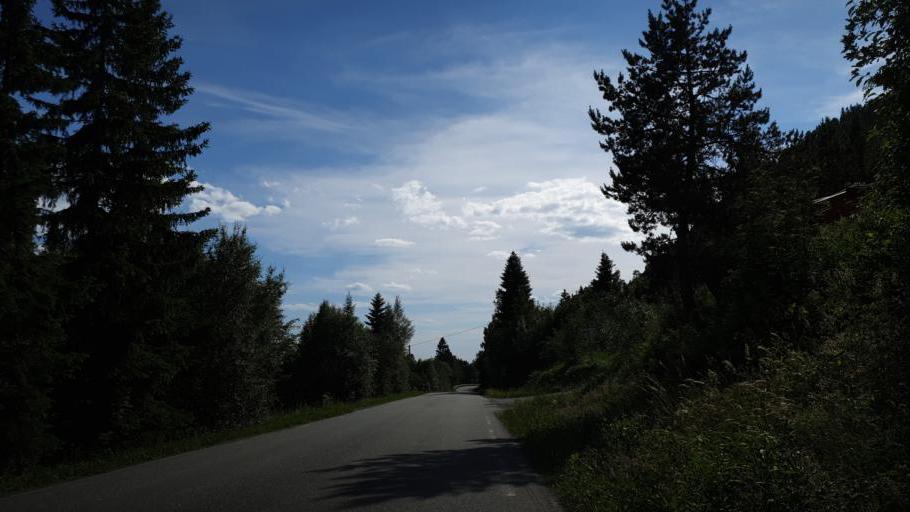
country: NO
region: Nord-Trondelag
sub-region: Leksvik
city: Leksvik
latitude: 63.6335
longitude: 10.5722
